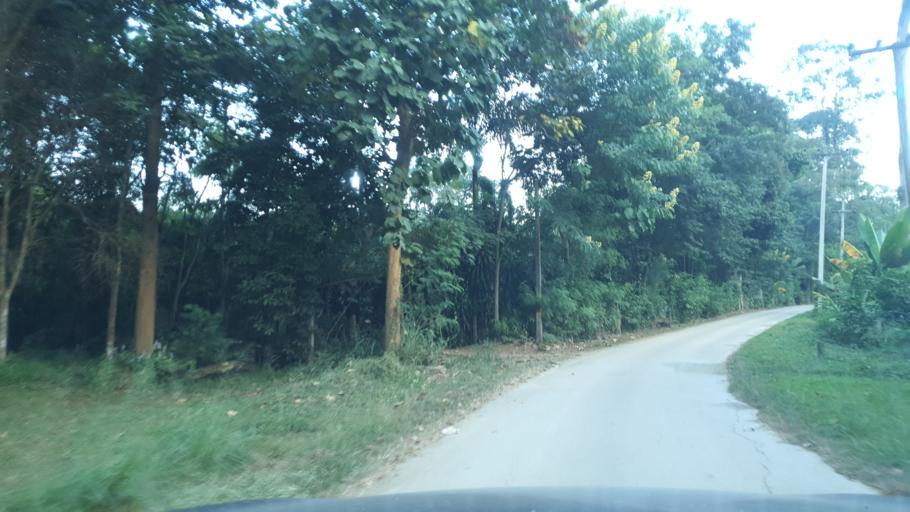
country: TH
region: Chiang Mai
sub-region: Amphoe Chiang Dao
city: Chiang Dao
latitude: 19.4042
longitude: 98.9238
